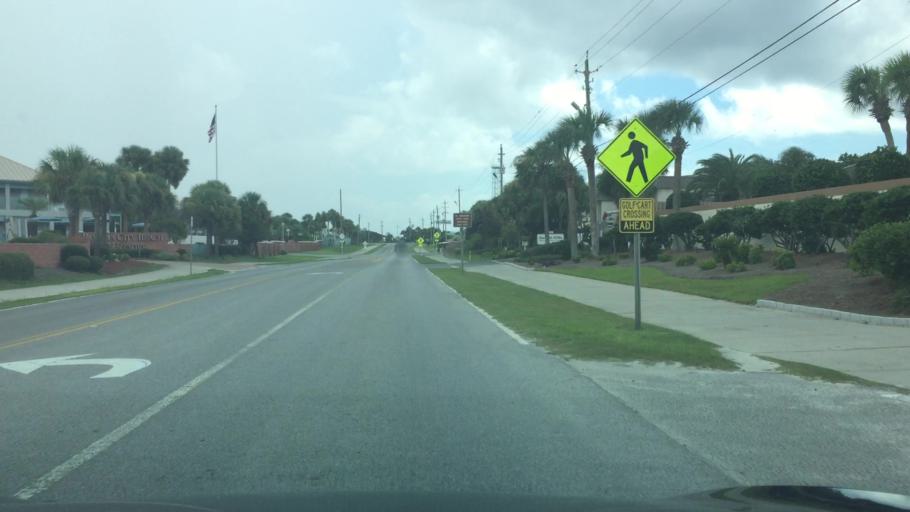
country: US
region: Florida
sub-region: Bay County
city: Lower Grand Lagoon
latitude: 30.1376
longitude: -85.7483
